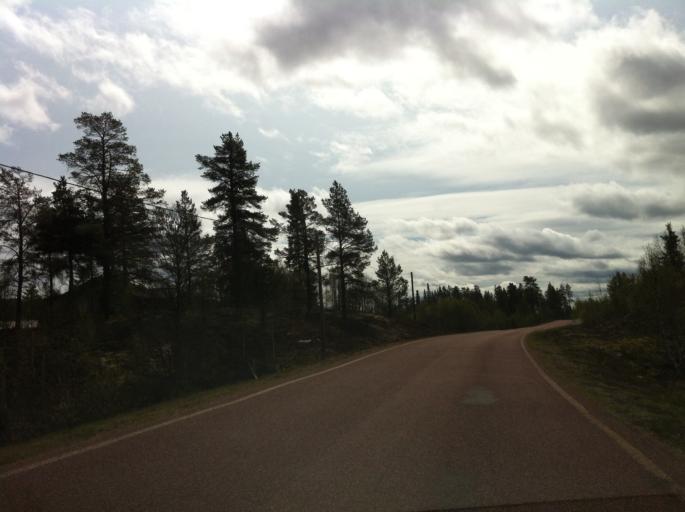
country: NO
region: Hedmark
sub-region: Engerdal
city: Engerdal
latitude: 62.1628
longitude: 12.9433
